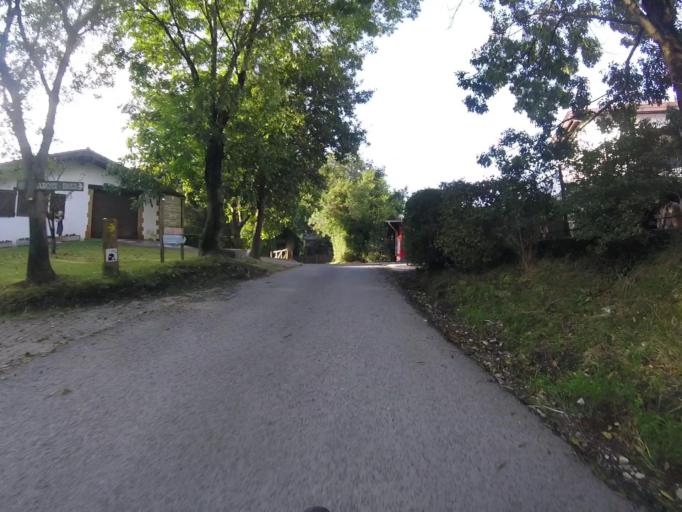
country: ES
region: Basque Country
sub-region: Provincia de Guipuzcoa
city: Fuenterrabia
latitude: 43.3594
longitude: -1.8113
